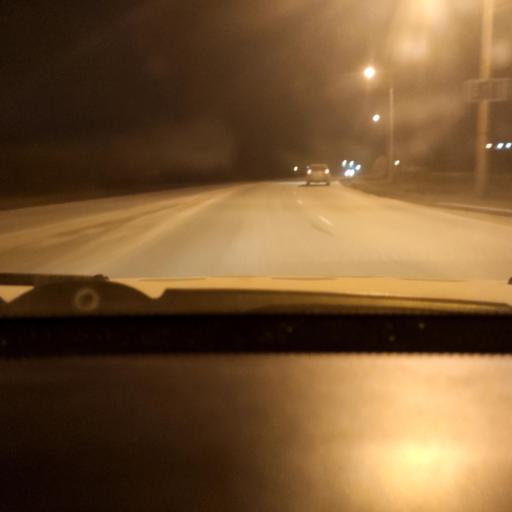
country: RU
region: Perm
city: Perm
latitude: 57.9625
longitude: 56.2032
